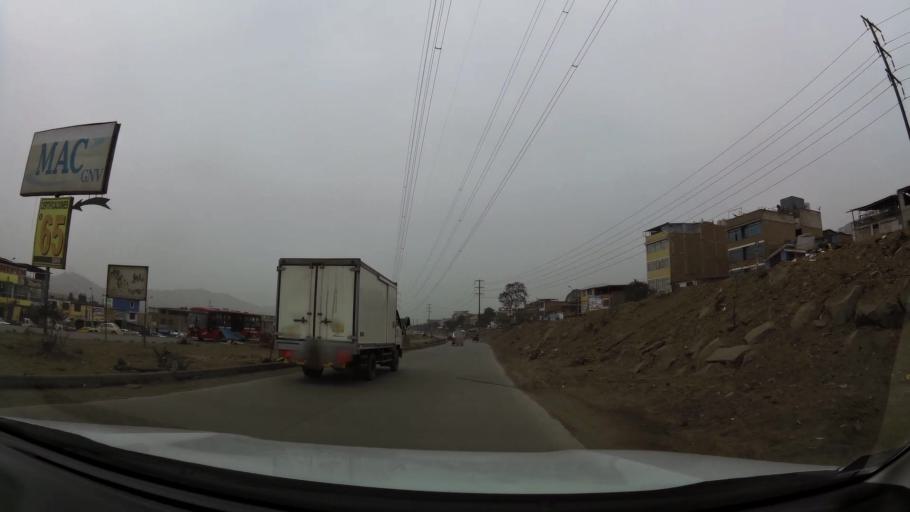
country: PE
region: Lima
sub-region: Lima
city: Surco
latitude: -12.1900
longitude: -76.9377
